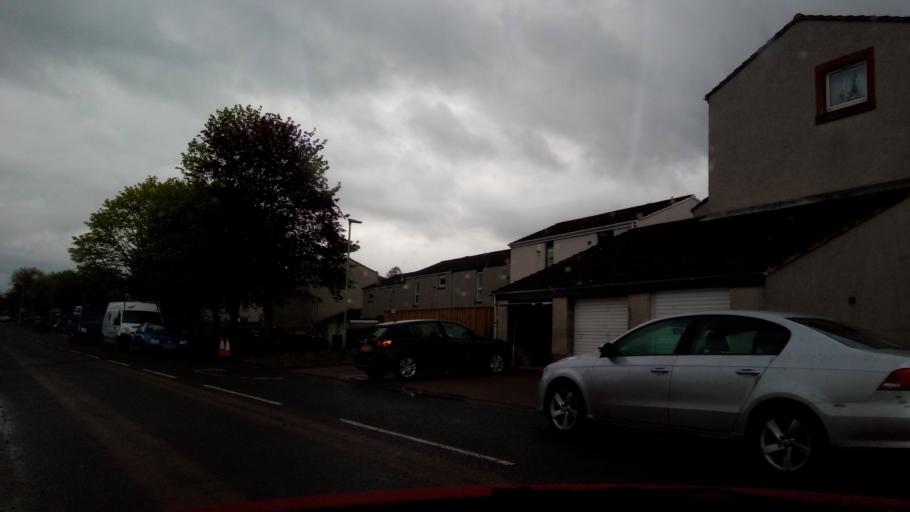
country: GB
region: Scotland
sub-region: The Scottish Borders
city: Jedburgh
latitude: 55.4728
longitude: -2.5461
